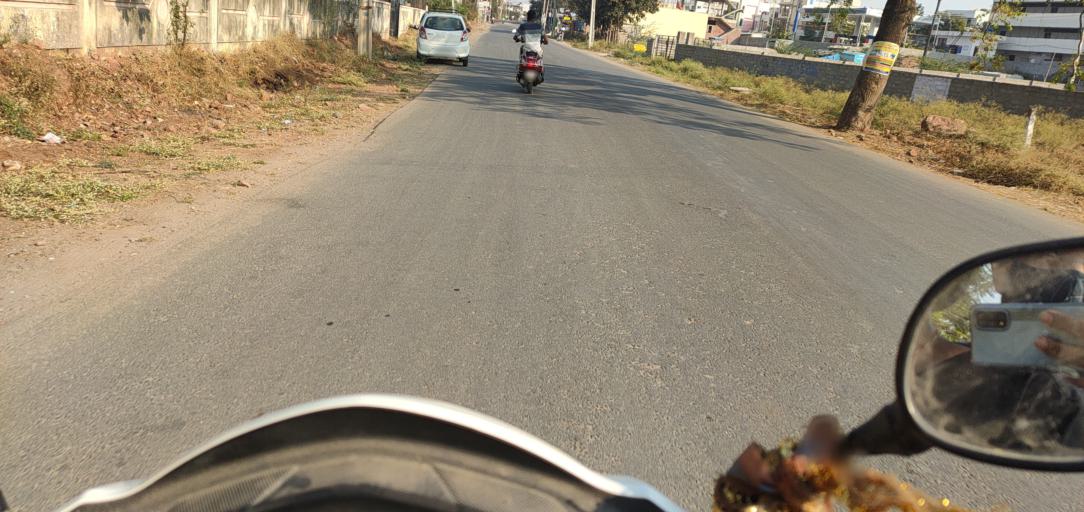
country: IN
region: Telangana
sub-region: Rangareddi
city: Lal Bahadur Nagar
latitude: 17.3404
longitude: 78.6230
